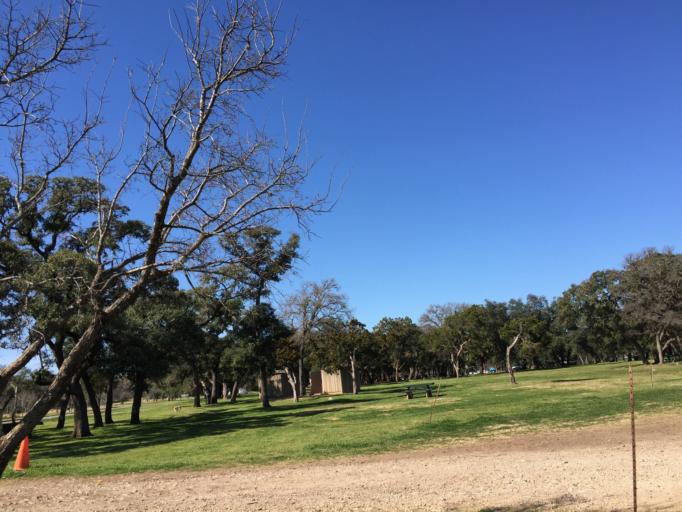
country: US
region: Texas
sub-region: Travis County
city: Rollingwood
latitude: 30.2664
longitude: -97.7732
